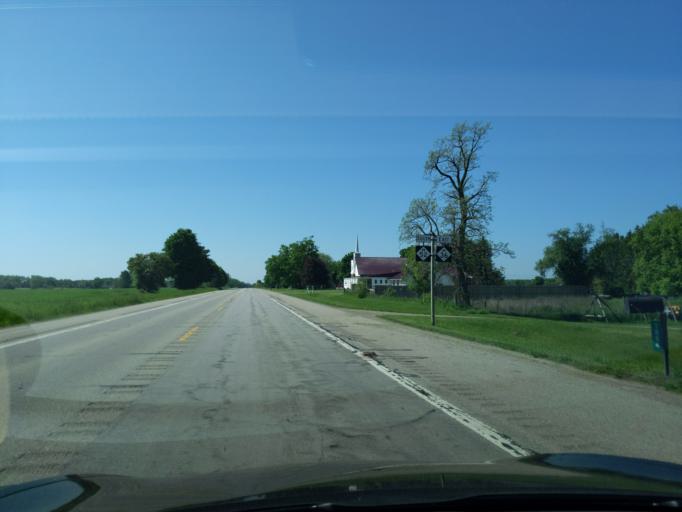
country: US
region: Michigan
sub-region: Ingham County
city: Stockbridge
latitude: 42.5293
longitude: -84.1908
